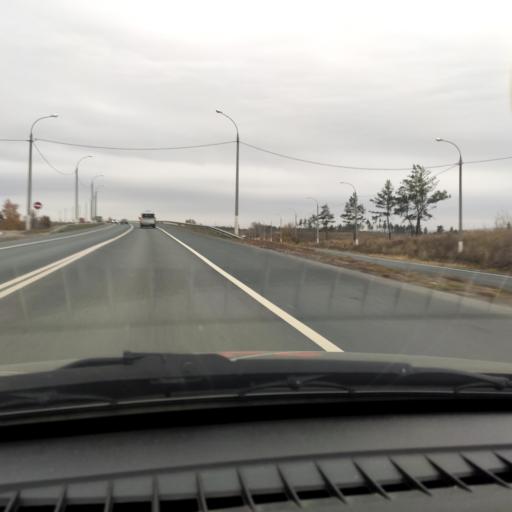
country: RU
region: Samara
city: Zhigulevsk
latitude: 53.5034
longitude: 49.5387
